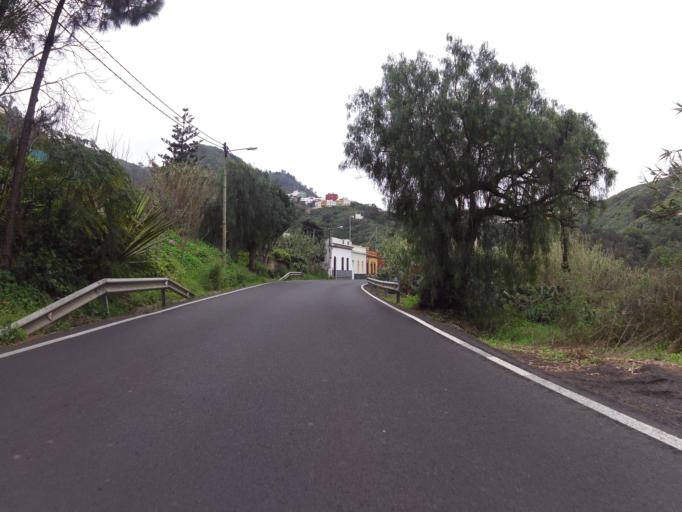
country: ES
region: Canary Islands
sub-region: Provincia de Las Palmas
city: Teror
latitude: 28.0703
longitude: -15.5249
